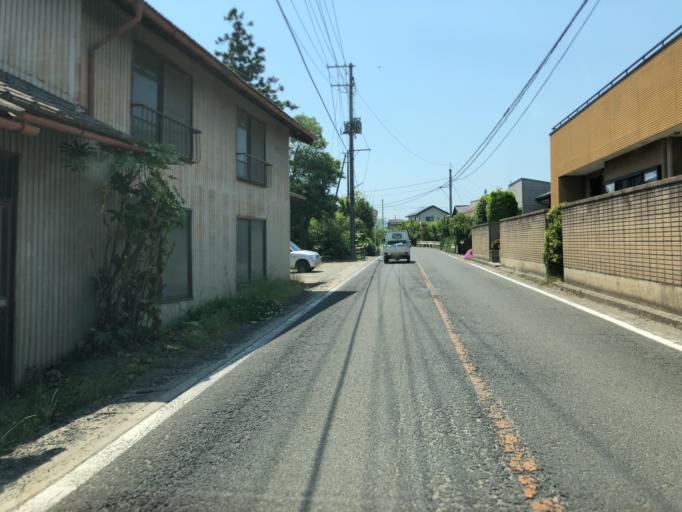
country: JP
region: Fukushima
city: Hobaramachi
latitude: 37.8264
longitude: 140.5324
